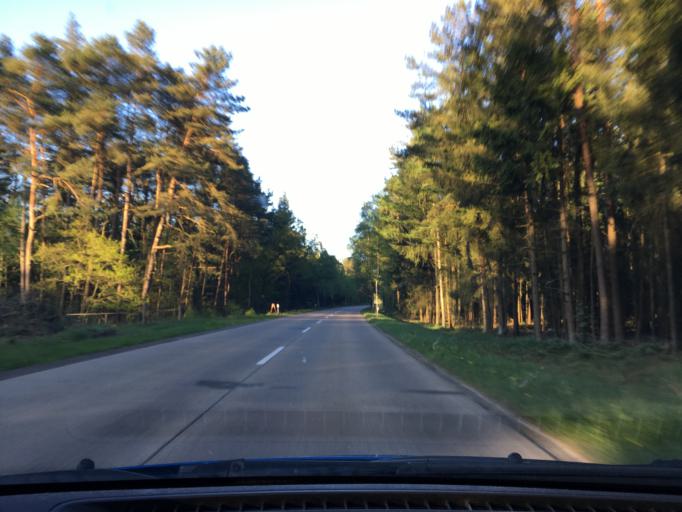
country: DE
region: Lower Saxony
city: Sudergellersen
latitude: 53.1837
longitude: 10.2770
